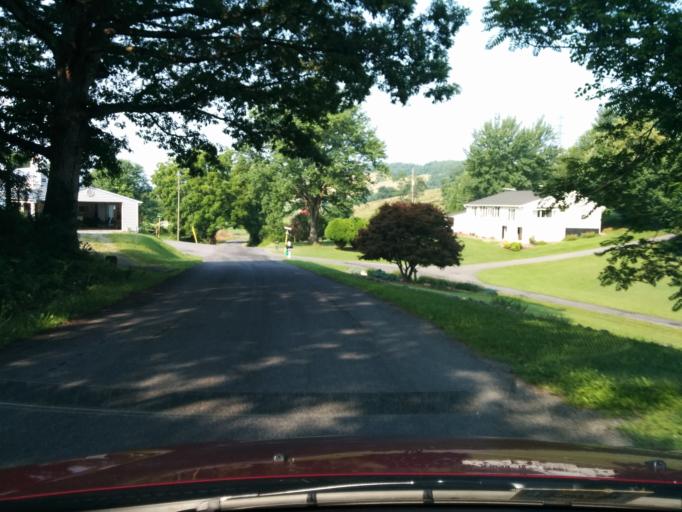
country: US
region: Virginia
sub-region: City of Lexington
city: Lexington
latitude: 37.7898
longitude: -79.5034
